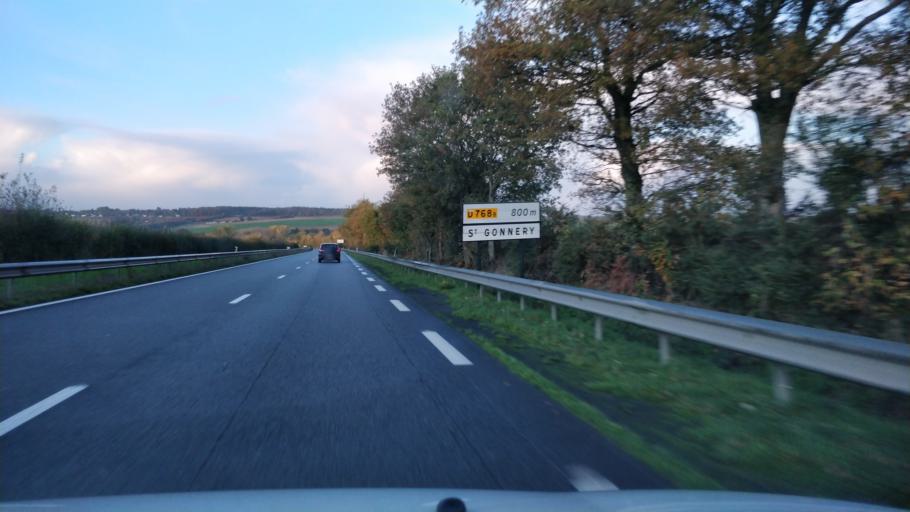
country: FR
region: Brittany
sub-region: Departement du Morbihan
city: Saint-Gonnery
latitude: 48.1410
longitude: -2.7838
